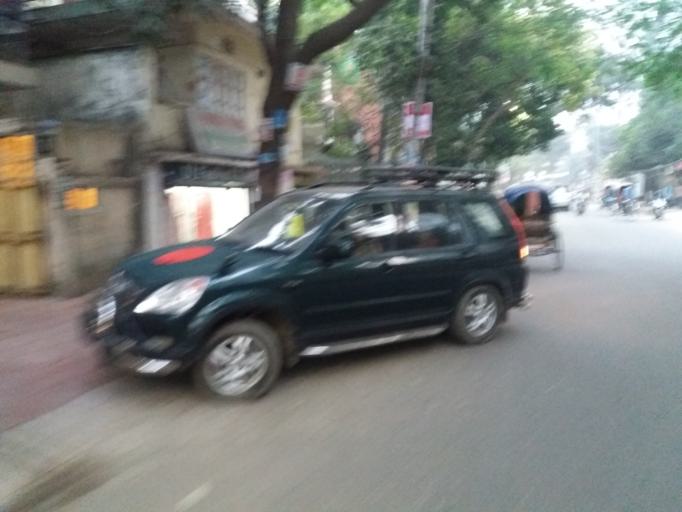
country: BD
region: Dhaka
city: Azimpur
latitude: 23.7478
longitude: 90.3731
